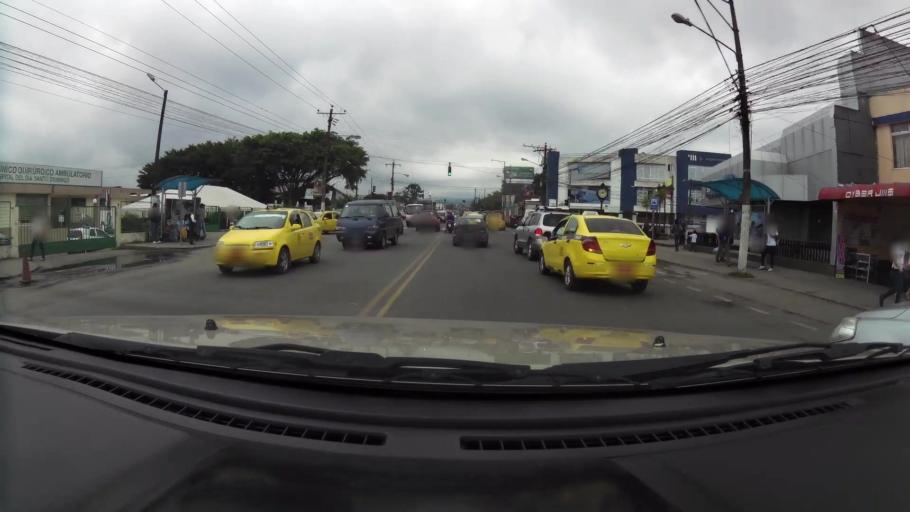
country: EC
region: Santo Domingo de los Tsachilas
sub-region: Canton Santo Domingo de los Colorados
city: Santo Domingo de los Colorados
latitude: -0.2483
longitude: -79.1569
